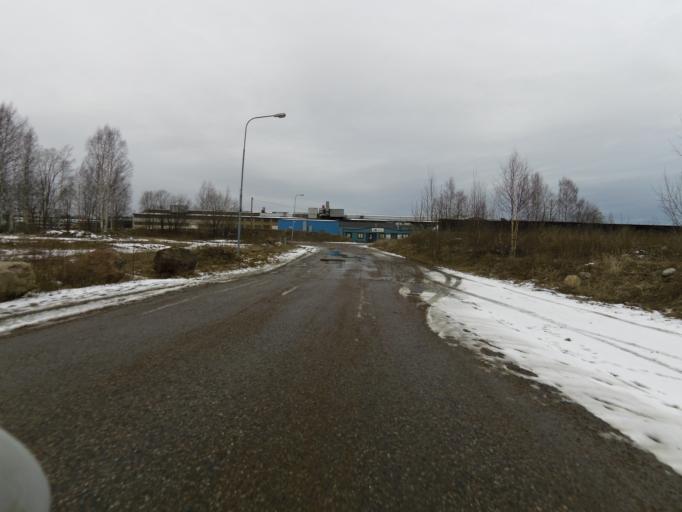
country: SE
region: Gaevleborg
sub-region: Gavle Kommun
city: Gavle
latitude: 60.6825
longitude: 17.1702
